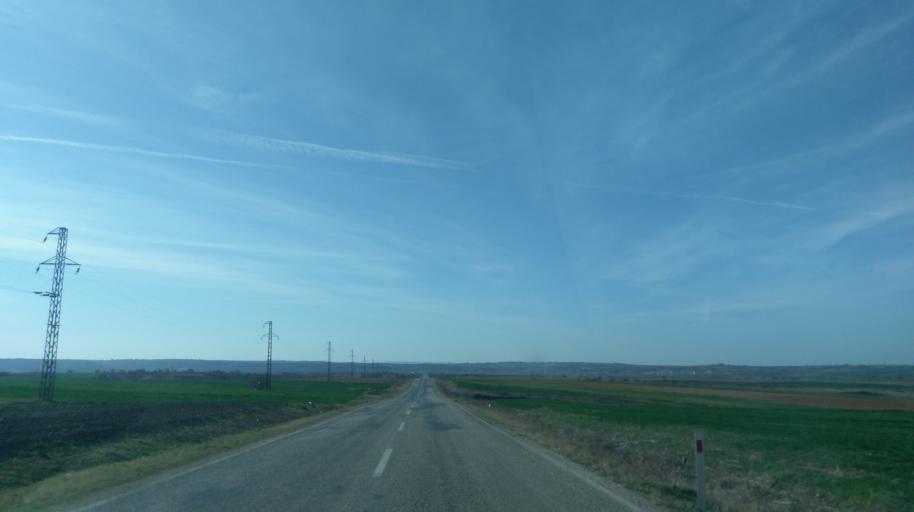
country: TR
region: Edirne
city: Copkoy
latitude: 41.2985
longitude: 26.8144
